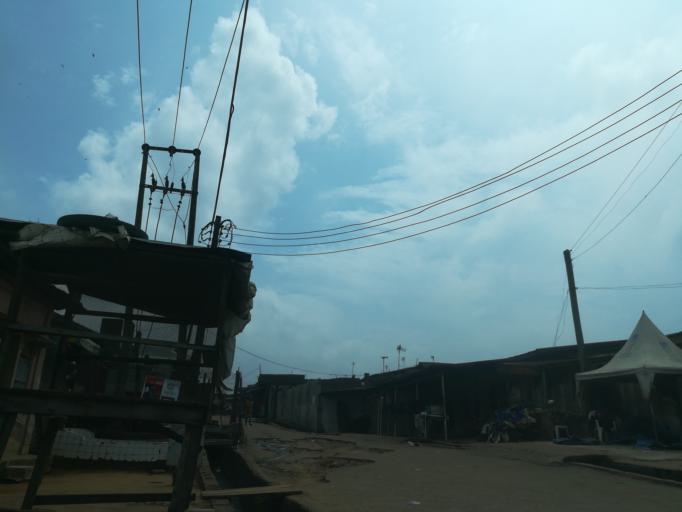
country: NG
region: Lagos
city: Ikorodu
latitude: 6.6112
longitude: 3.5041
